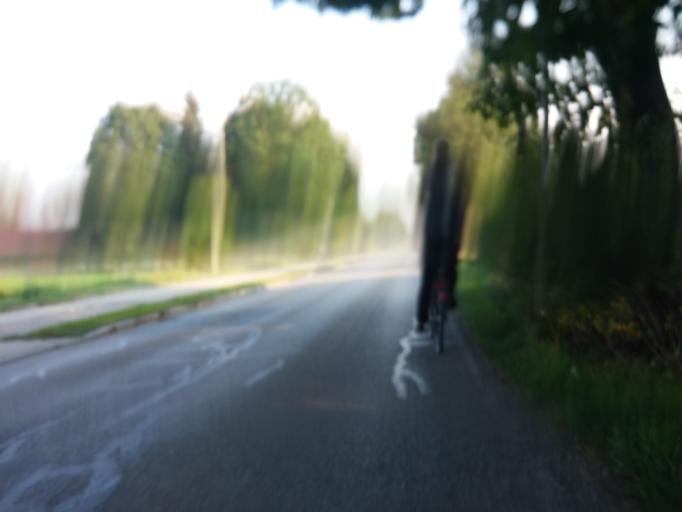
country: DE
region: Bavaria
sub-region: Upper Bavaria
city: Kirchheim bei Muenchen
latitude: 48.1695
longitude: 11.7796
